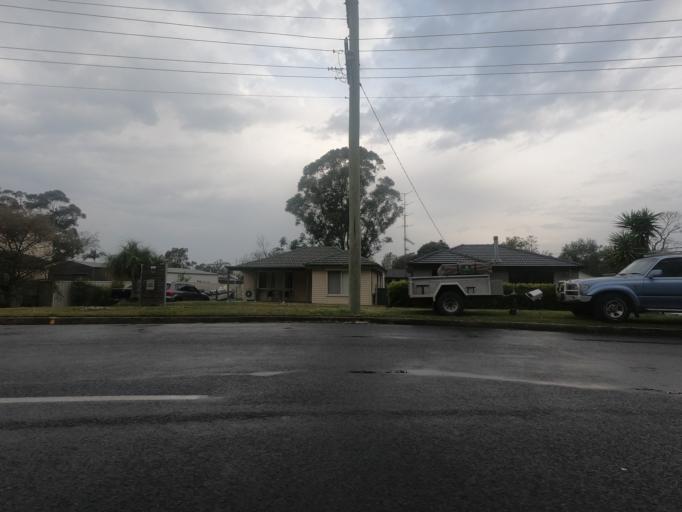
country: AU
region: New South Wales
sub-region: Wollongong
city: Koonawarra
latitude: -34.4957
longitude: 150.8048
